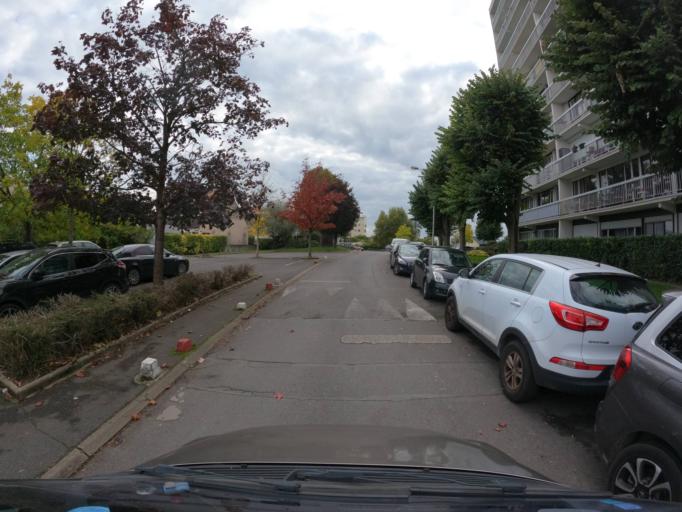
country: FR
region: Ile-de-France
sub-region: Departement de Seine-et-Marne
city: Chelles
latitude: 48.8840
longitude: 2.5834
